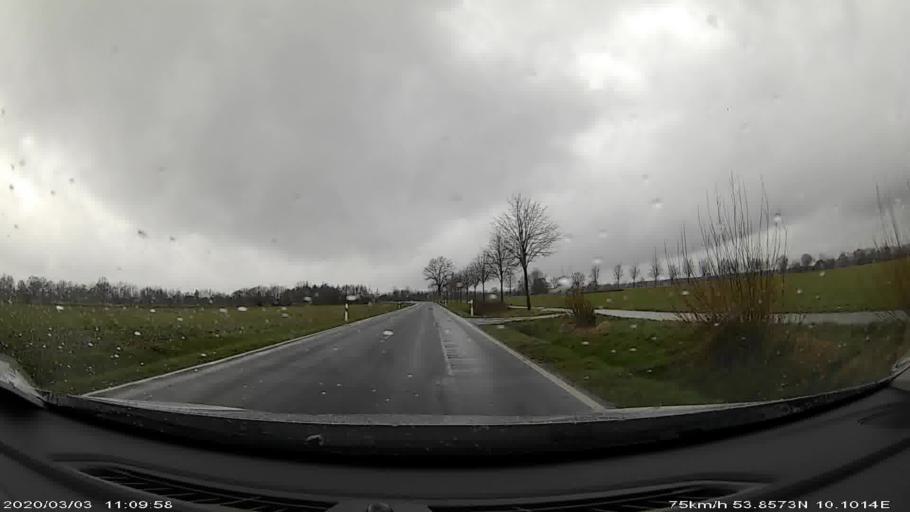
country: DE
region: Schleswig-Holstein
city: Sievershutten
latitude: 53.8590
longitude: 10.0983
